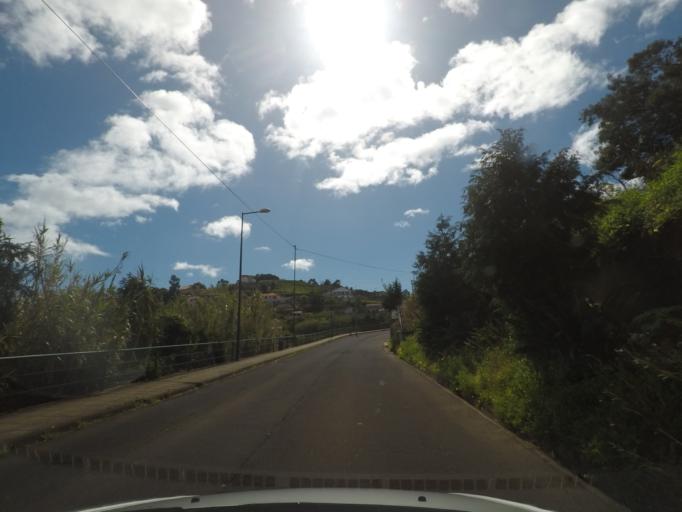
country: PT
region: Madeira
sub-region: Santa Cruz
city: Camacha
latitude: 32.6592
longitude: -16.8521
